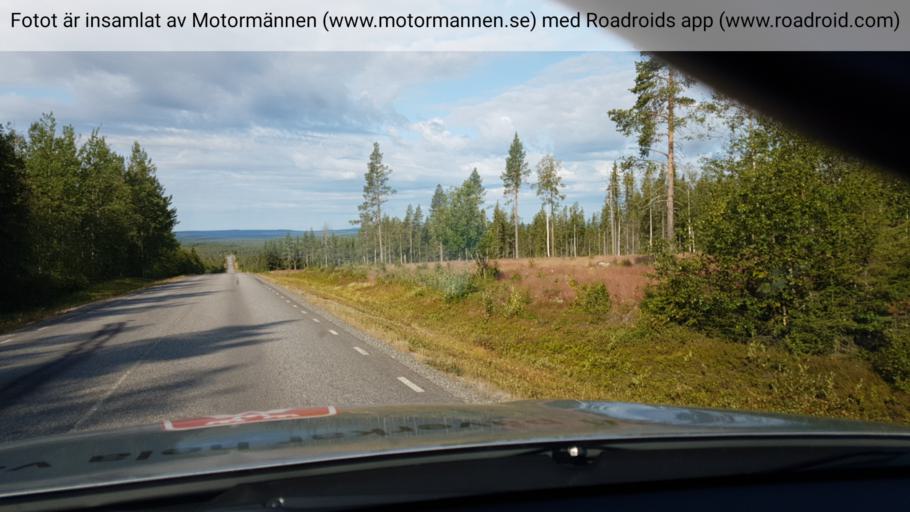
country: SE
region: Vaesterbotten
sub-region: Skelleftea Kommun
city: Storvik
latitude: 65.3262
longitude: 20.7345
